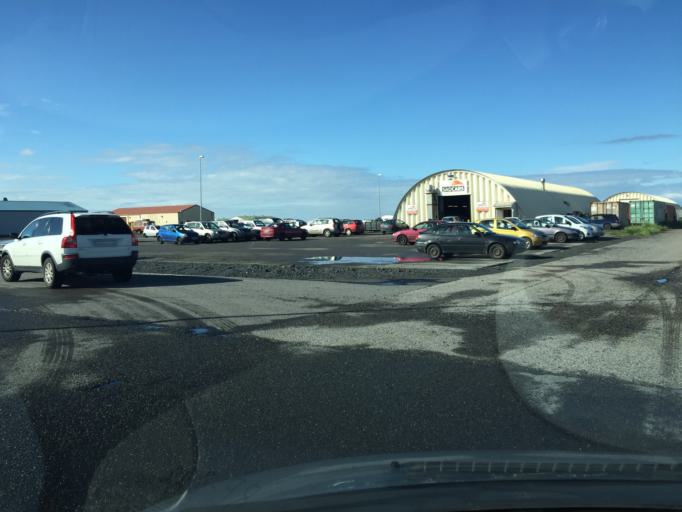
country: IS
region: Southern Peninsula
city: Reykjanesbaer
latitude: 63.9663
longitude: -22.5753
